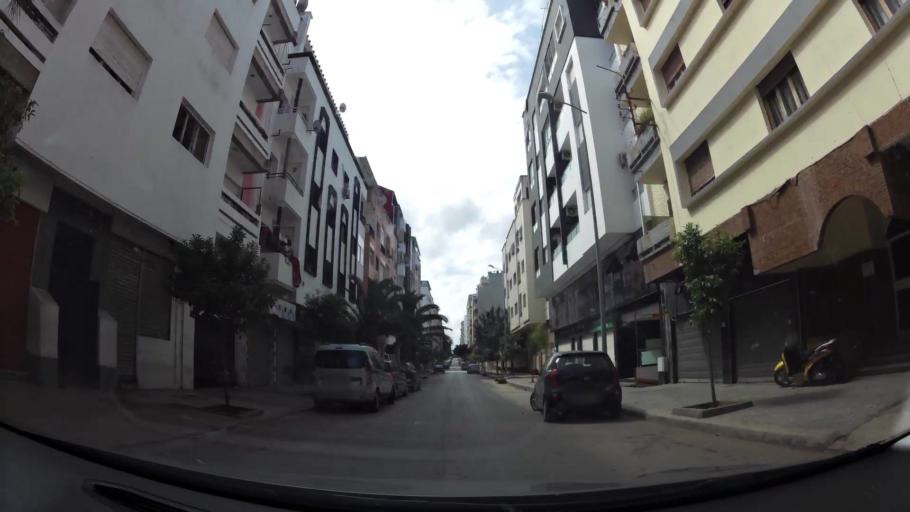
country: MA
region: Gharb-Chrarda-Beni Hssen
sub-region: Kenitra Province
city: Kenitra
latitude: 34.2587
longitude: -6.5828
